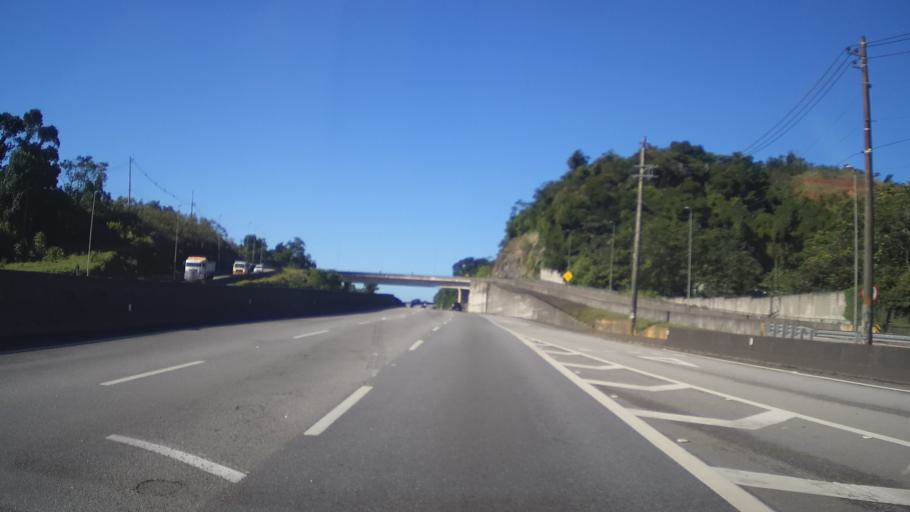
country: BR
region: Sao Paulo
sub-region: Cubatao
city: Cubatao
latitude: -23.9229
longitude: -46.4601
